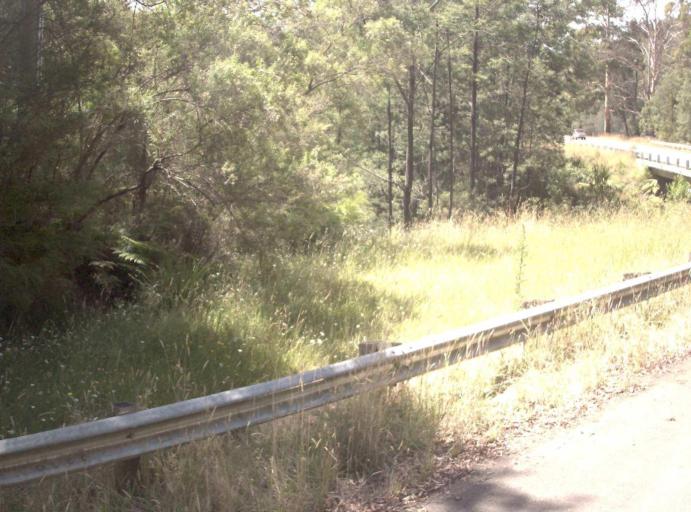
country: AU
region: Victoria
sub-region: Baw Baw
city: Warragul
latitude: -37.9076
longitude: 146.0224
